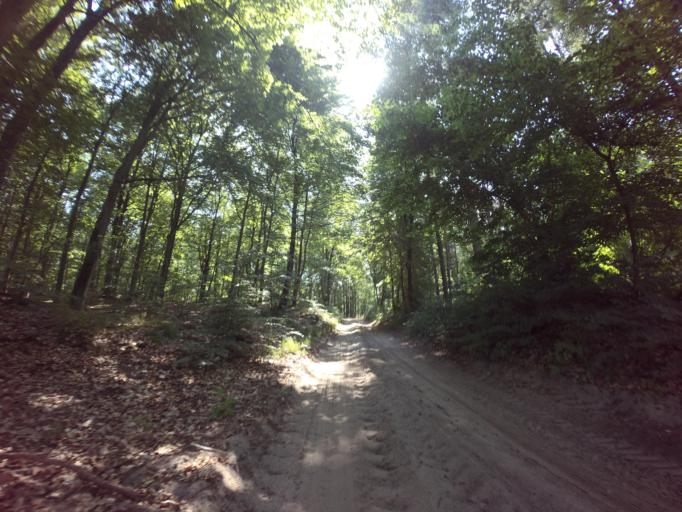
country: PL
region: West Pomeranian Voivodeship
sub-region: Powiat choszczenski
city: Bierzwnik
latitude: 53.0905
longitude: 15.7504
